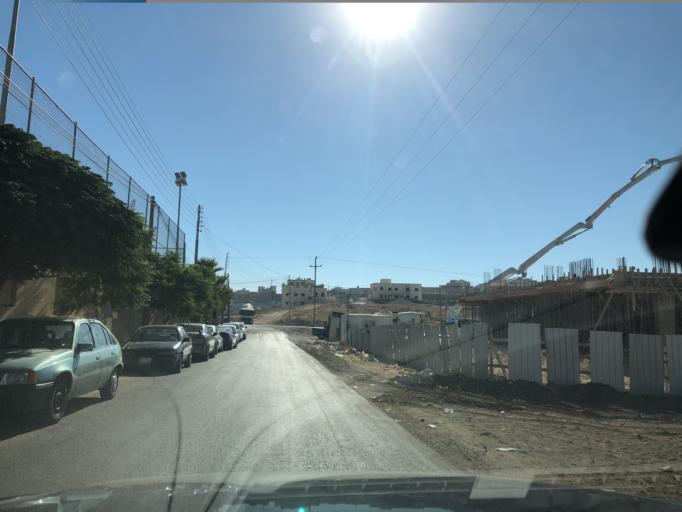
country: JO
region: Amman
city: Wadi as Sir
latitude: 31.9305
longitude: 35.8432
